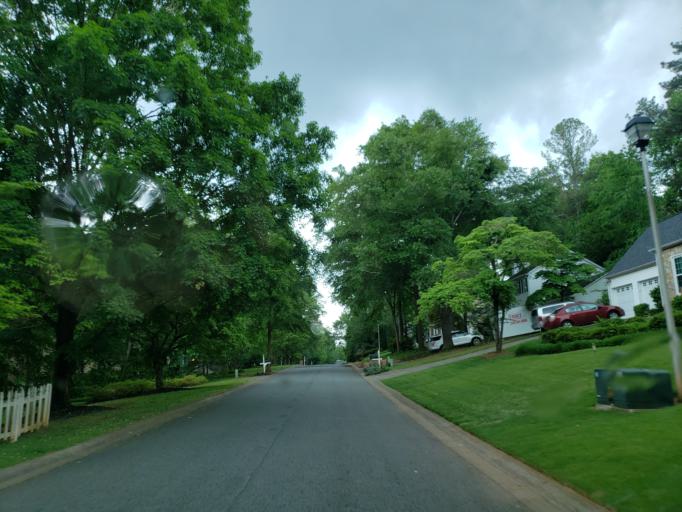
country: US
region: Georgia
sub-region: Cobb County
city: Marietta
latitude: 33.9581
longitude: -84.5707
